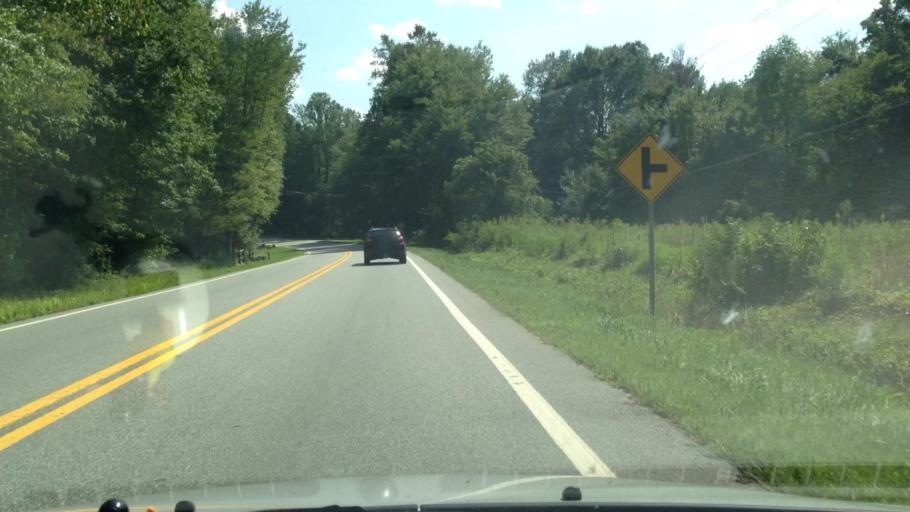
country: US
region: North Carolina
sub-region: Guilford County
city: Oak Ridge
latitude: 36.1804
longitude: -79.9885
